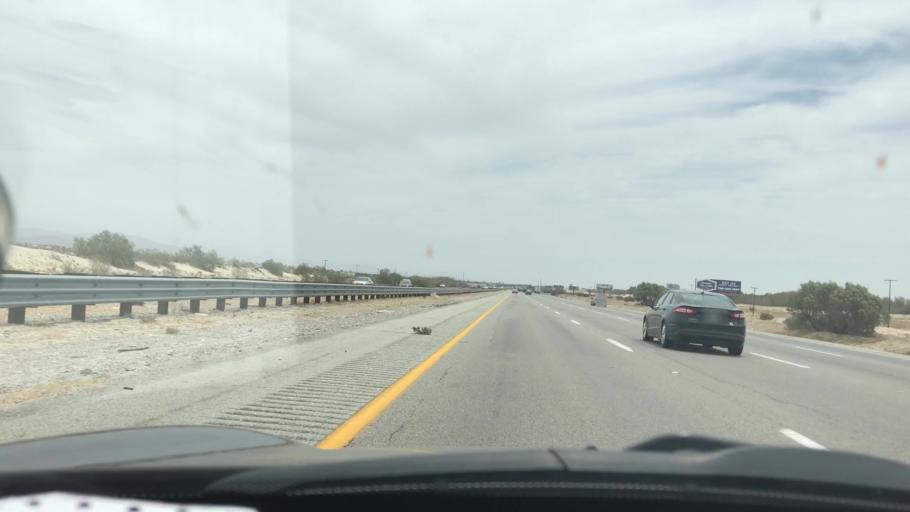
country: US
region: California
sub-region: Riverside County
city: Thousand Palms
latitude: 33.8325
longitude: -116.4300
